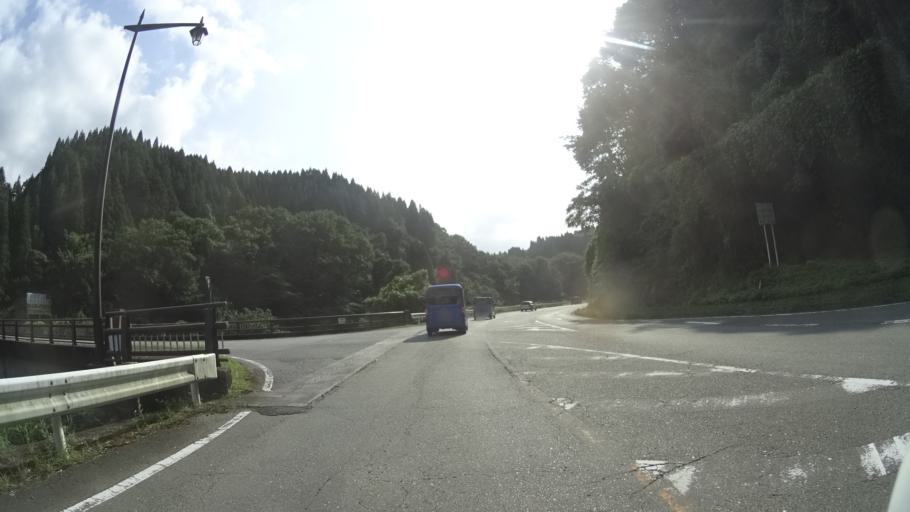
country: JP
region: Kumamoto
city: Aso
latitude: 32.6848
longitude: 131.0591
